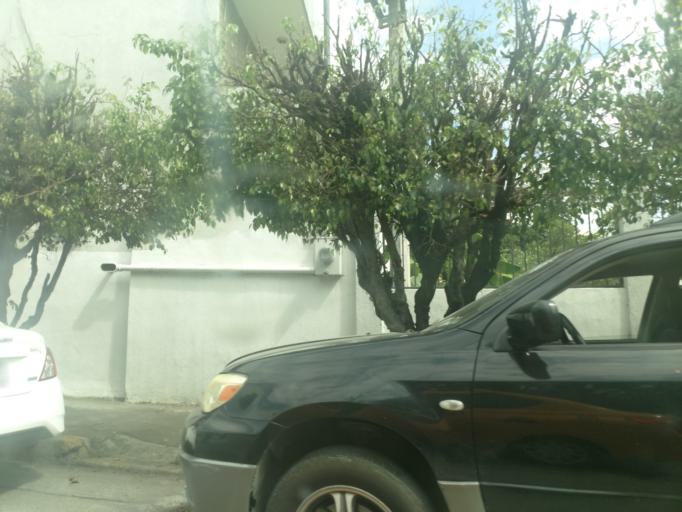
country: MX
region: Nayarit
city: Tepic
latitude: 21.4999
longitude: -104.8821
